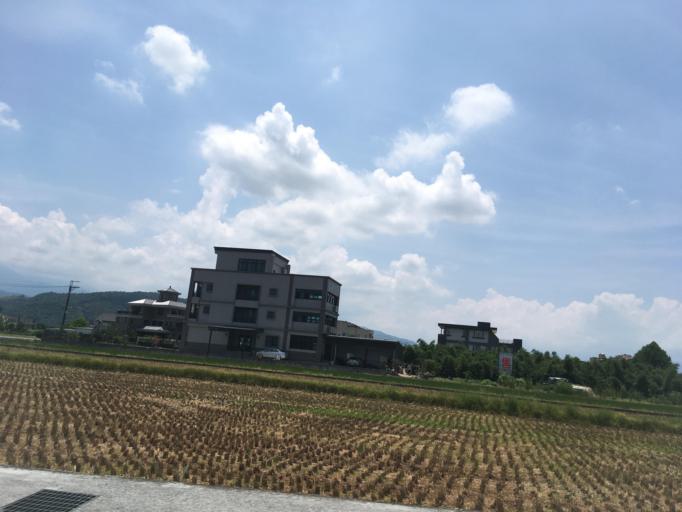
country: TW
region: Taiwan
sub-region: Yilan
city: Yilan
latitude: 24.6508
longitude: 121.7635
